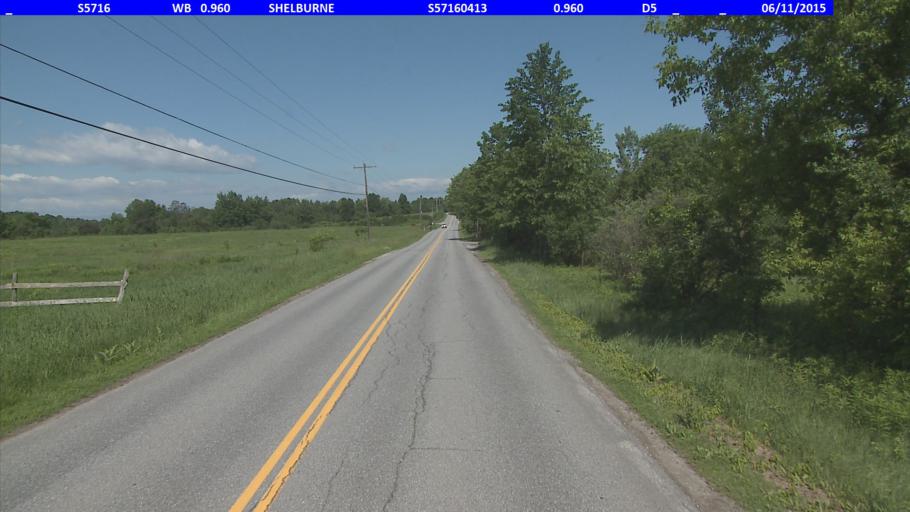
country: US
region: Vermont
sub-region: Chittenden County
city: Hinesburg
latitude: 44.3720
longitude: -73.1931
